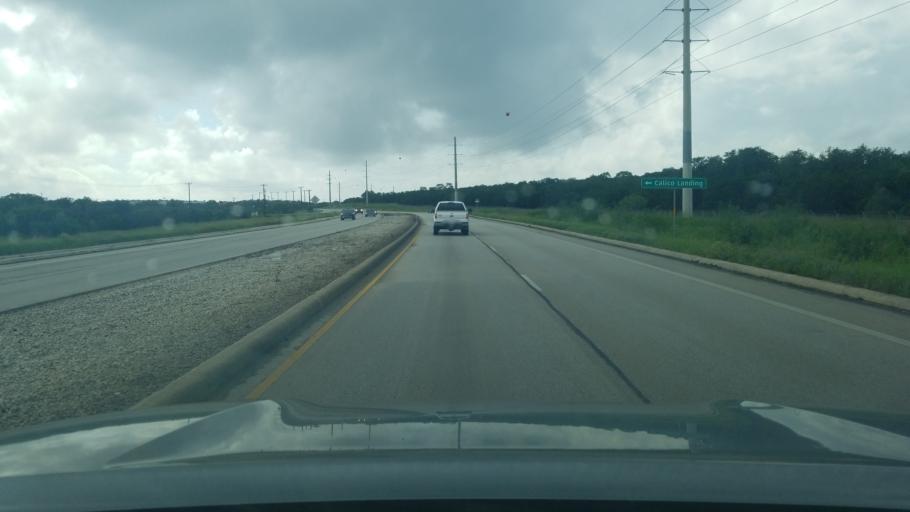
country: US
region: Texas
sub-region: Bexar County
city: Hollywood Park
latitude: 29.6555
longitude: -98.5211
